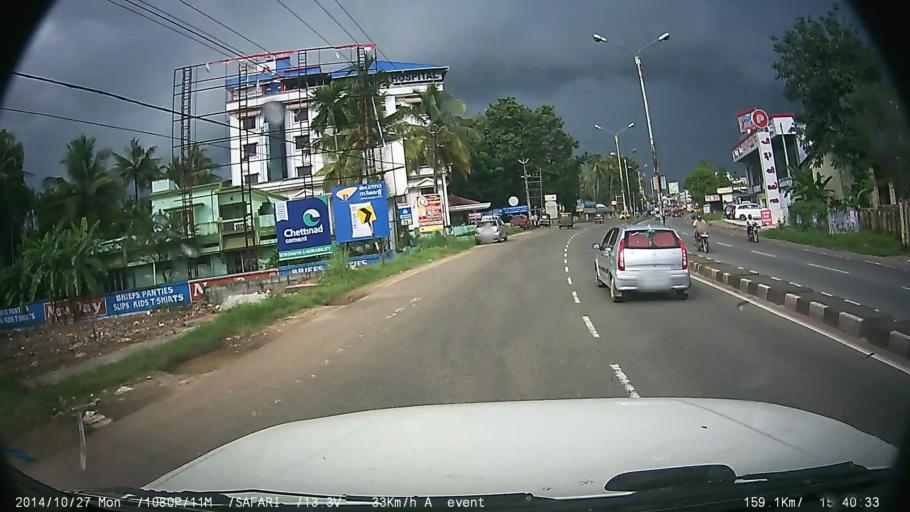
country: IN
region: Kerala
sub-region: Ernakulam
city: Angamali
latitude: 10.1876
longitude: 76.3819
